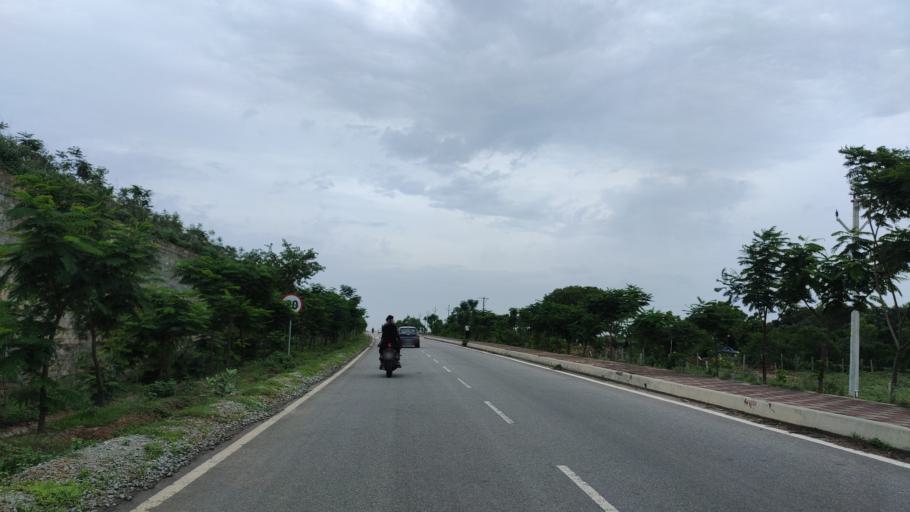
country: IN
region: Telangana
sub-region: Rangareddi
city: Secunderabad
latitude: 17.5796
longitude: 78.5911
